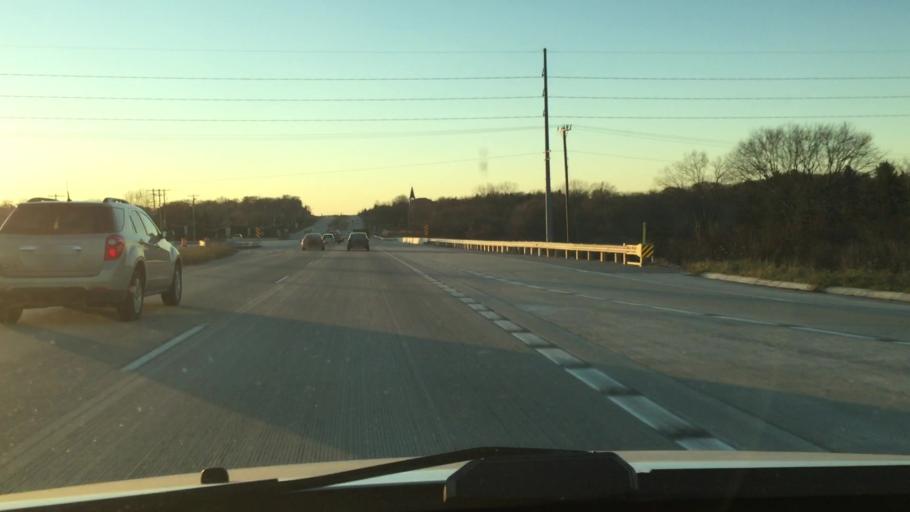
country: US
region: Wisconsin
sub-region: Waukesha County
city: Sussex
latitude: 43.0831
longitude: -88.2038
